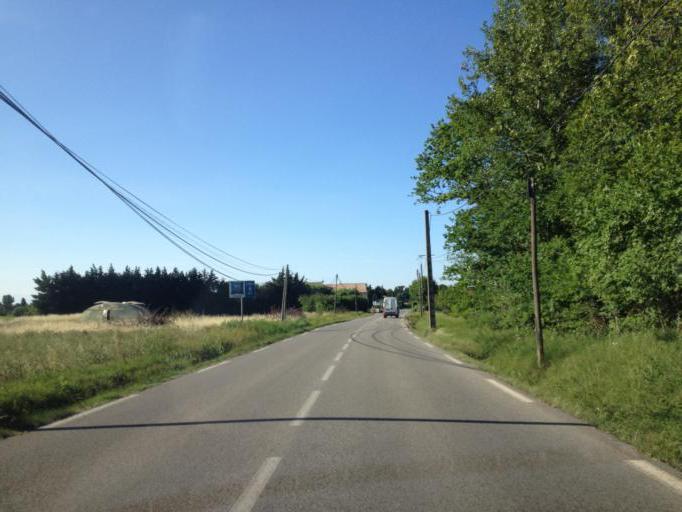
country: FR
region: Provence-Alpes-Cote d'Azur
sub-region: Departement du Vaucluse
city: Caderousse
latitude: 44.1066
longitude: 4.7913
